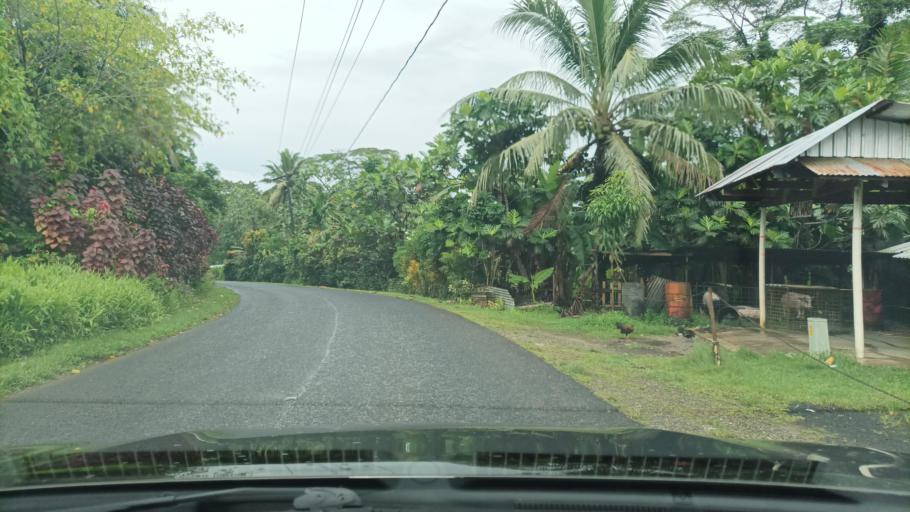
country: FM
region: Pohnpei
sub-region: Sokehs Municipality
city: Palikir - National Government Center
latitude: 6.9187
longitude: 158.1607
